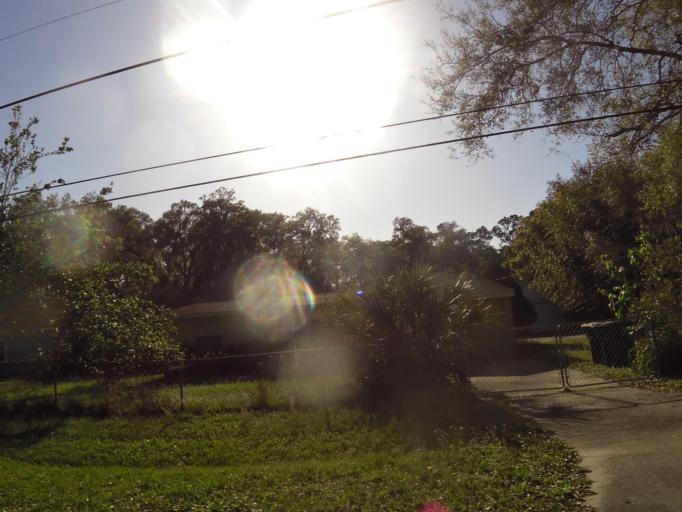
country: US
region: Florida
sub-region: Duval County
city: Jacksonville
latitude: 30.2762
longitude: -81.5771
